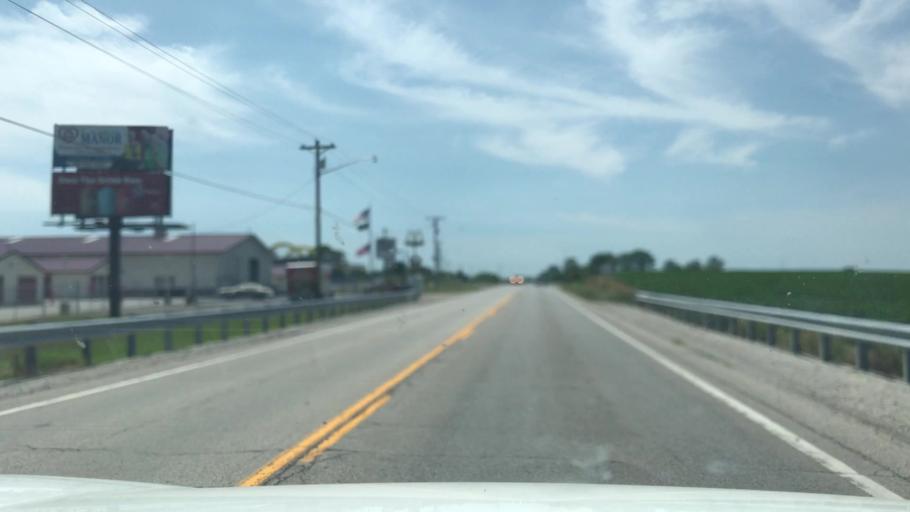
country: US
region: Illinois
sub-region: Clinton County
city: New Baden
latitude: 38.5354
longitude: -89.7191
